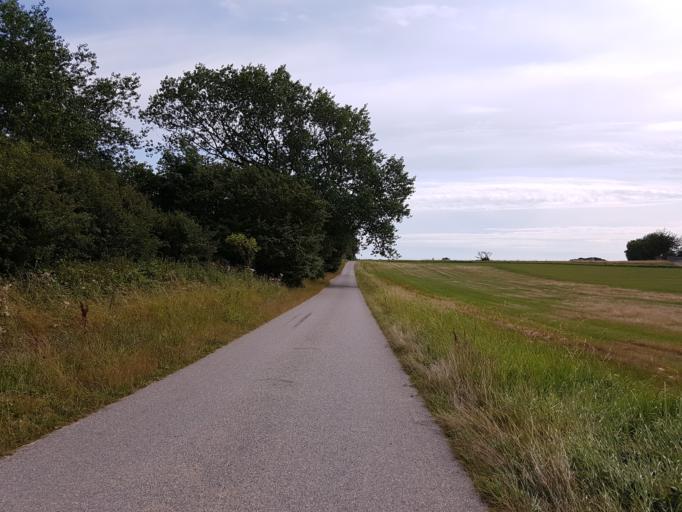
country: DK
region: Zealand
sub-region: Guldborgsund Kommune
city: Nykobing Falster
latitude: 54.5745
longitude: 11.9689
